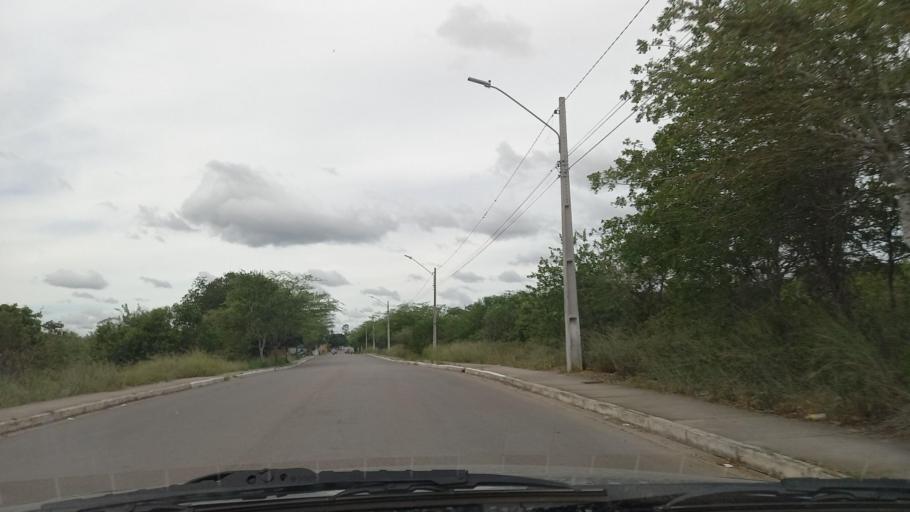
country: BR
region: Pernambuco
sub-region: Gravata
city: Gravata
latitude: -8.2086
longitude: -35.5917
